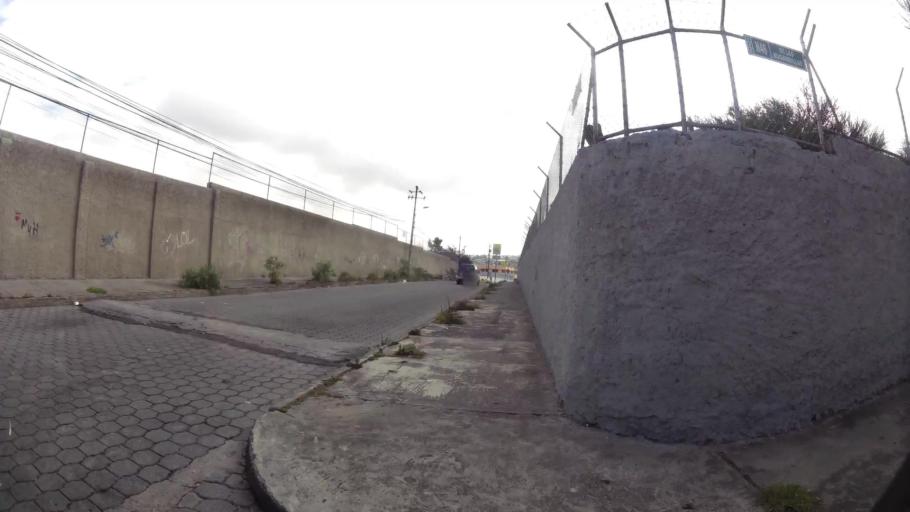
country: EC
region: Pichincha
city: Quito
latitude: -0.1591
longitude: -78.4706
